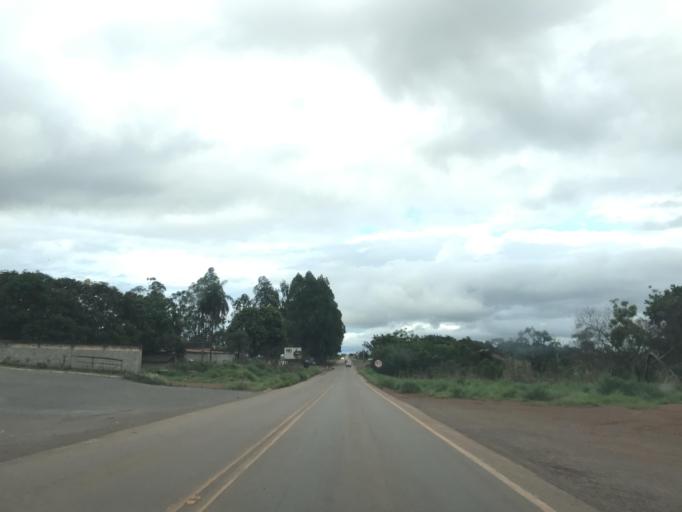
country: BR
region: Goias
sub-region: Luziania
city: Luziania
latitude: -16.4641
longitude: -48.2137
